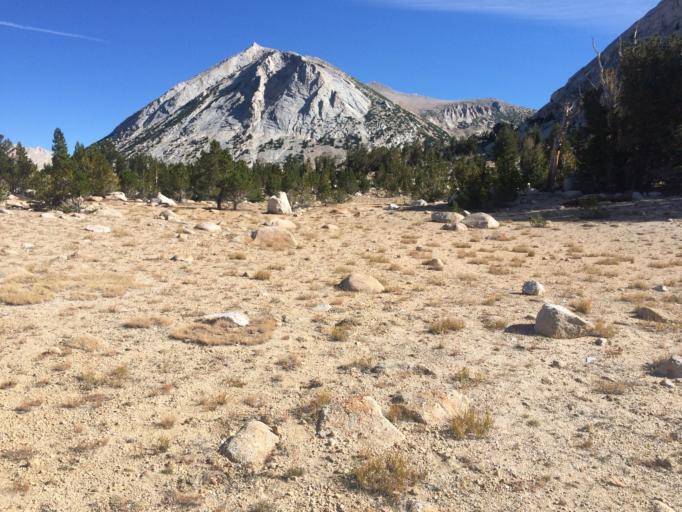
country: US
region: California
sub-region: Mariposa County
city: Yosemite Valley
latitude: 37.9379
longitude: -119.3343
